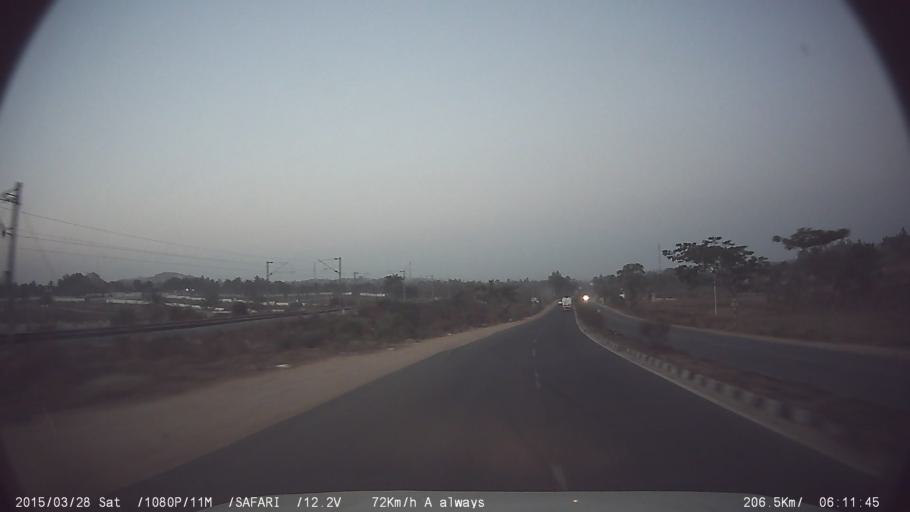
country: IN
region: Karnataka
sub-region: Ramanagara
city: Ramanagaram
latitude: 12.7811
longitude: 77.3698
